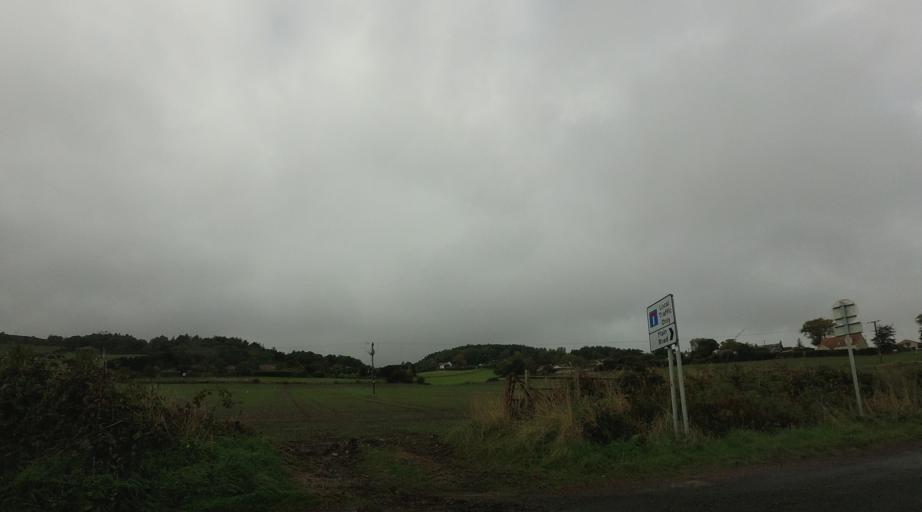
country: GB
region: Scotland
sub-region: Fife
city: Balmullo
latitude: 56.3859
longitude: -2.9284
